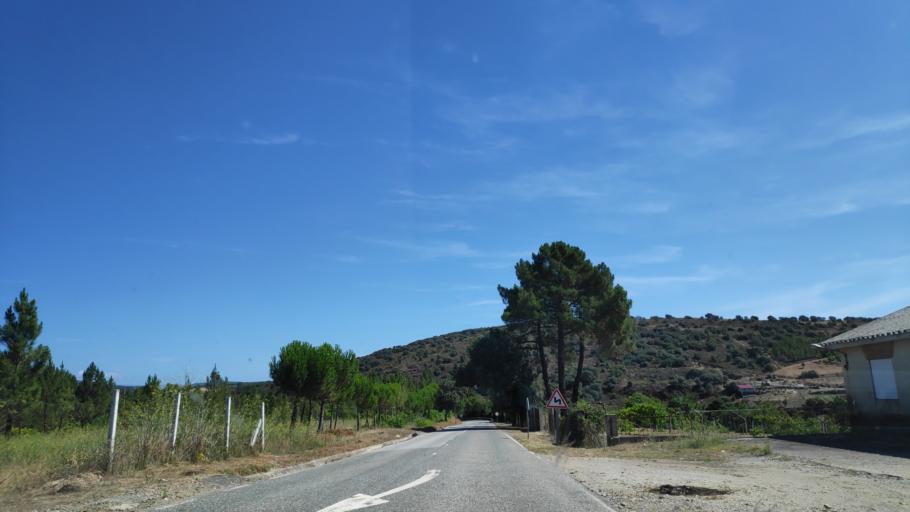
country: PT
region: Braganca
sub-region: Braganca Municipality
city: Braganca
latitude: 41.8282
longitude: -6.7480
